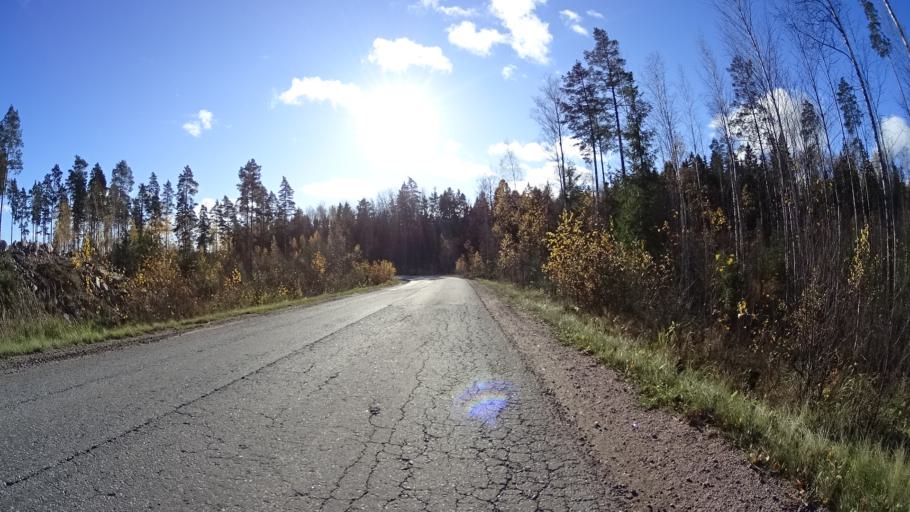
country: FI
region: Uusimaa
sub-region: Helsinki
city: Kilo
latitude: 60.3089
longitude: 24.8386
